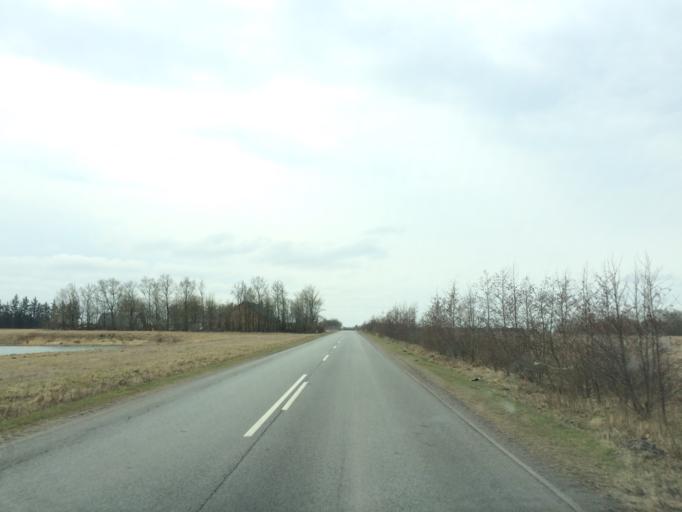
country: DK
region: Central Jutland
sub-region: Ringkobing-Skjern Kommune
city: Tarm
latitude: 55.8440
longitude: 8.4746
